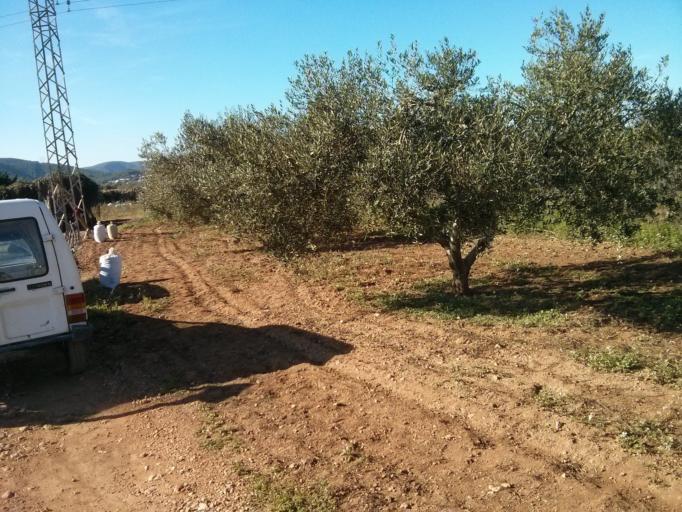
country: ES
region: Catalonia
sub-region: Provincia de Tarragona
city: Santa Oliva
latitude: 41.2471
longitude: 1.5418
